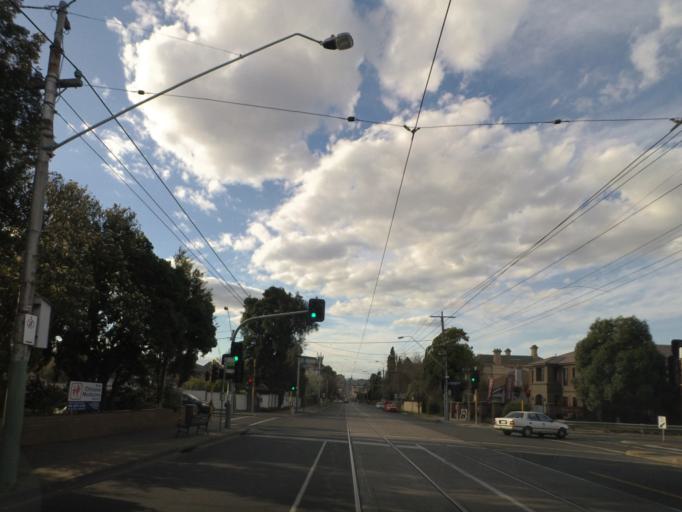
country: AU
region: Victoria
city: Glenferrie
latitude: -37.8356
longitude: 145.0558
